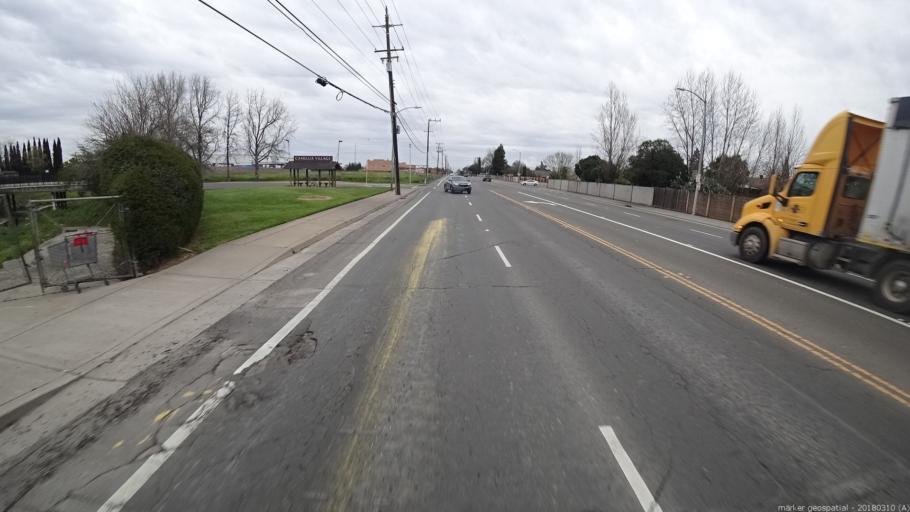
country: US
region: California
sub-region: Sacramento County
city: Florin
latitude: 38.4818
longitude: -121.4026
